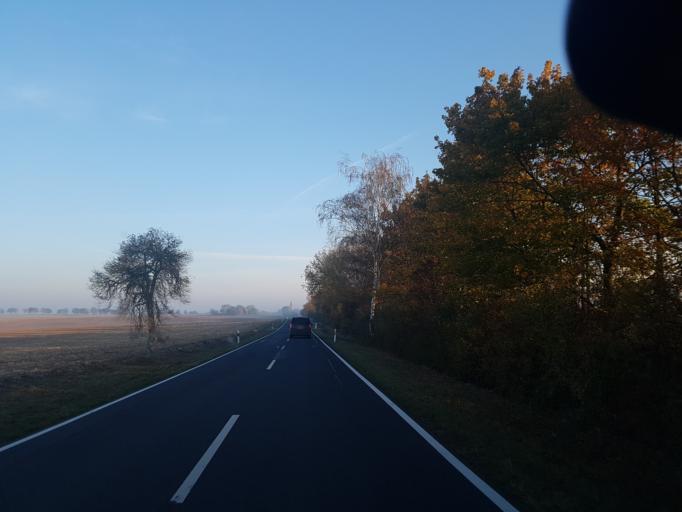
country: DE
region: Brandenburg
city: Juterbog
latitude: 51.9362
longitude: 13.0872
